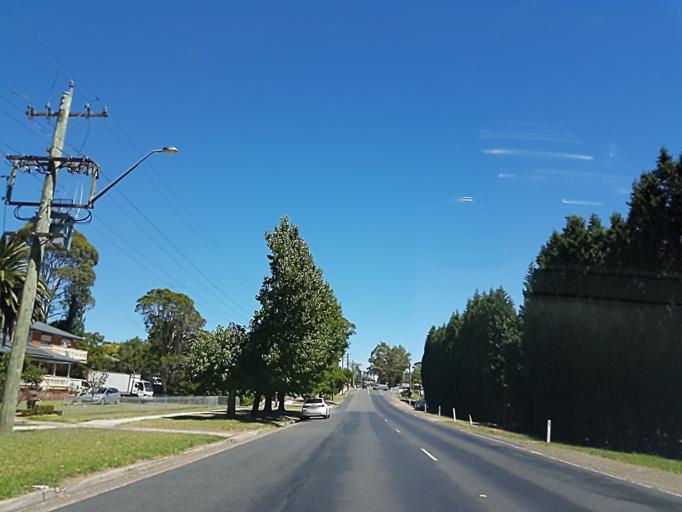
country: AU
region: New South Wales
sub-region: Hornsby Shire
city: Glenorie
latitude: -33.6033
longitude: 151.0107
